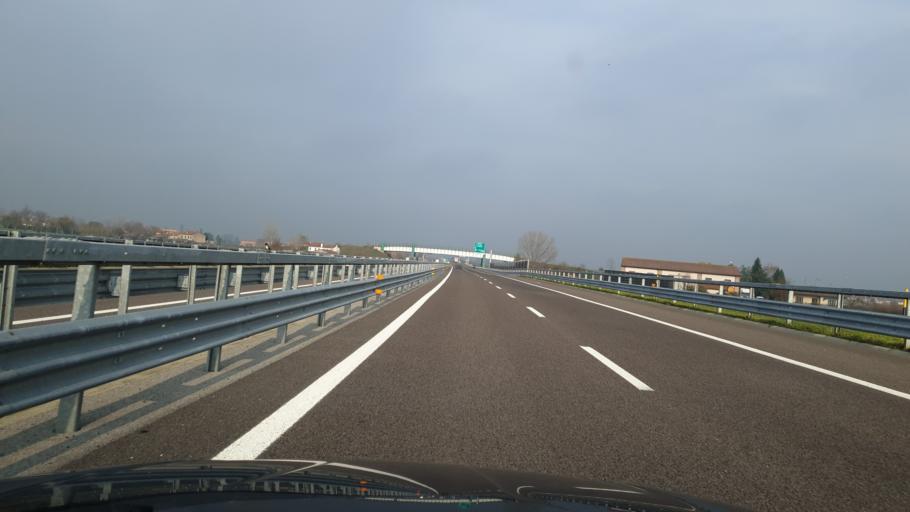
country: IT
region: Veneto
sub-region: Provincia di Padova
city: Megliadino San Vitale
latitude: 45.1961
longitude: 11.5432
